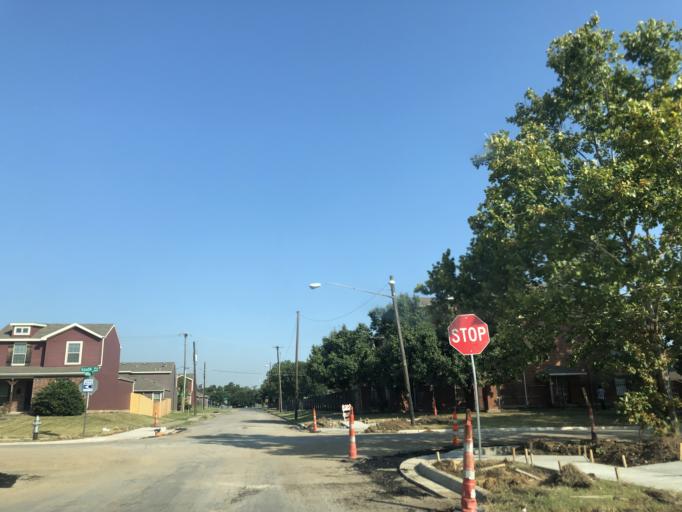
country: US
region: Texas
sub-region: Dallas County
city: Dallas
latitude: 32.7708
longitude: -96.7681
